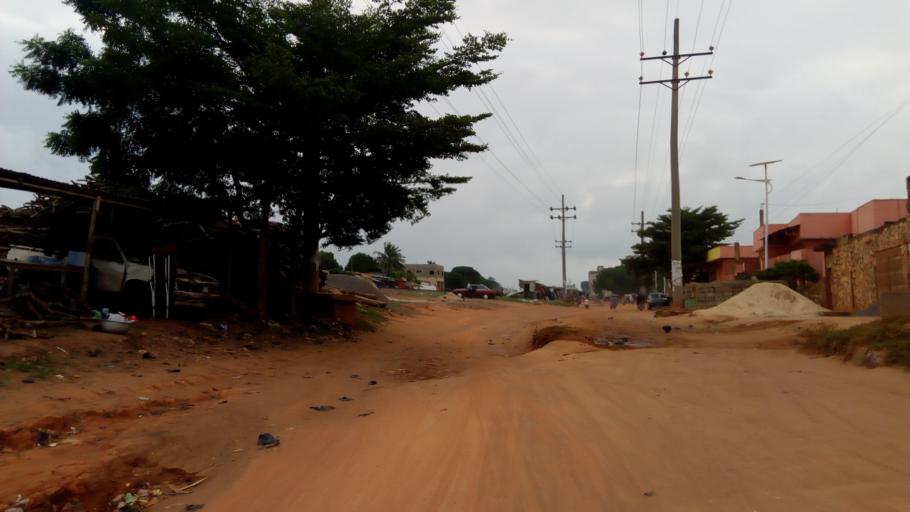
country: TG
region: Maritime
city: Lome
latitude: 6.1624
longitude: 1.2068
